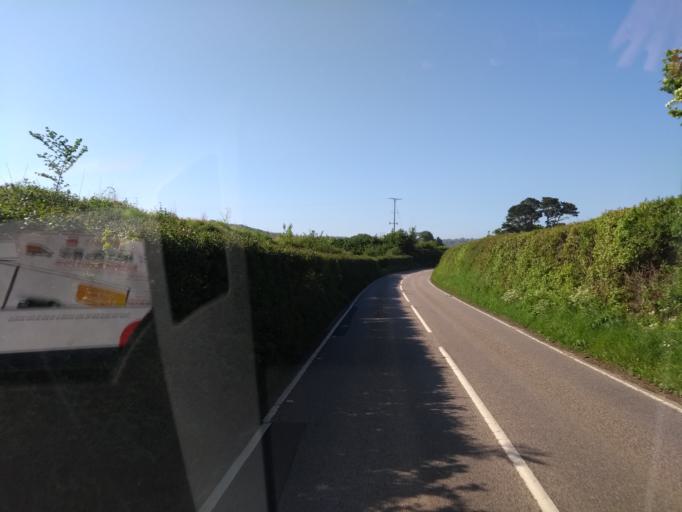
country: GB
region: England
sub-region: Somerset
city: Taunton
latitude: 50.9820
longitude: -3.0891
